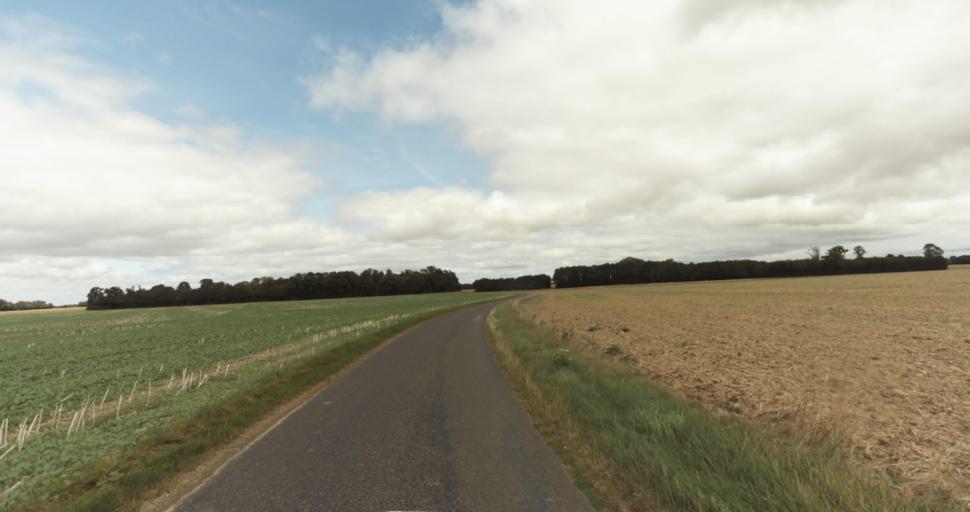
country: FR
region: Haute-Normandie
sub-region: Departement de l'Eure
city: La Madeleine-de-Nonancourt
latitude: 48.8962
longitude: 1.1993
